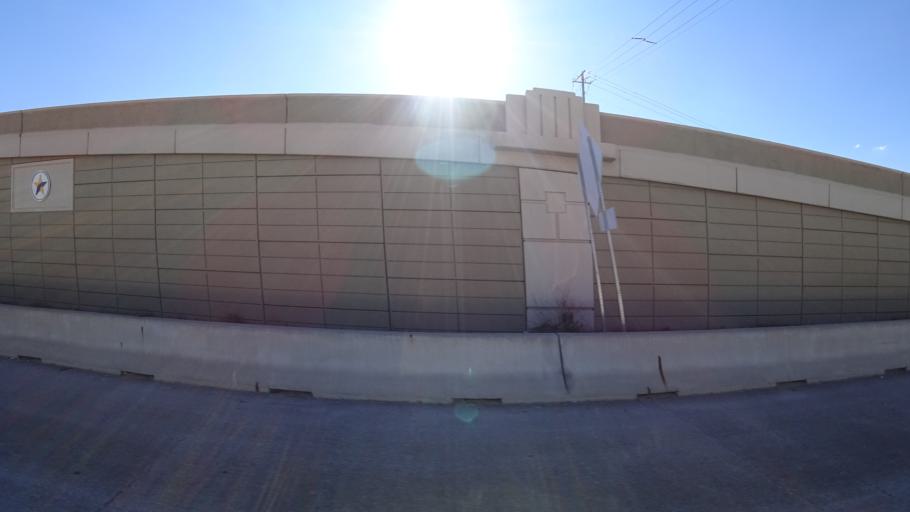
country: US
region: Texas
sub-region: Travis County
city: Austin
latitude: 30.3279
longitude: -97.6769
